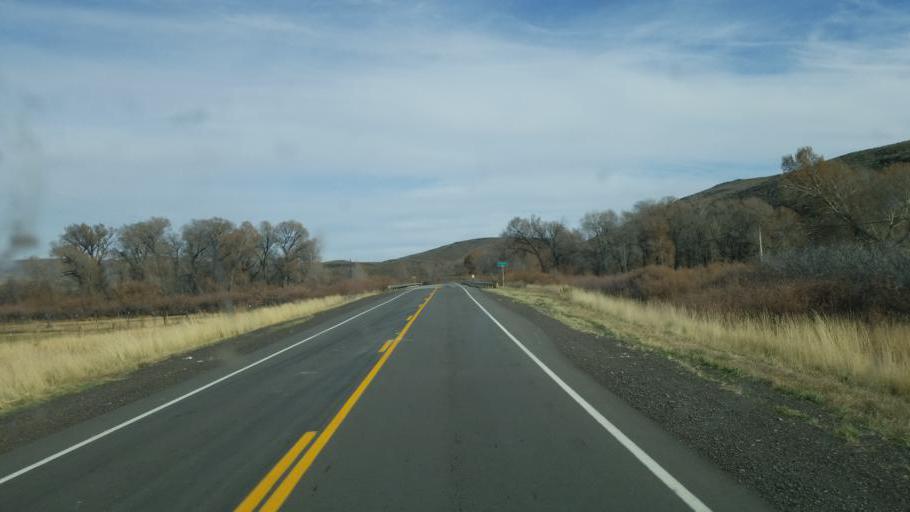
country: US
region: Colorado
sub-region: Conejos County
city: Conejos
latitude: 37.1737
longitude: -105.8994
